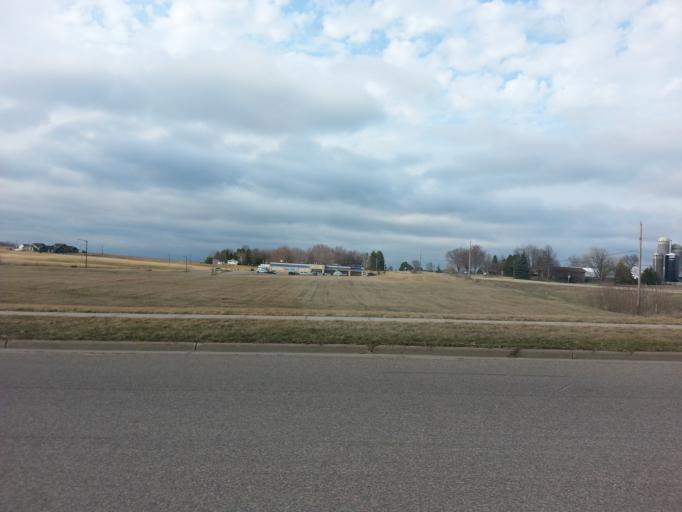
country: US
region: Wisconsin
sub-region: Pierce County
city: Ellsworth
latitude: 44.7464
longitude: -92.4877
